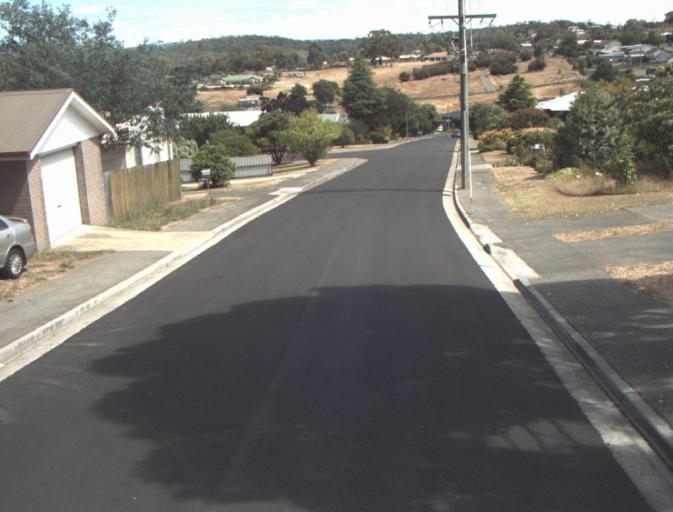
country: AU
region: Tasmania
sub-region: Launceston
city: Summerhill
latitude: -41.4617
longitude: 147.1300
